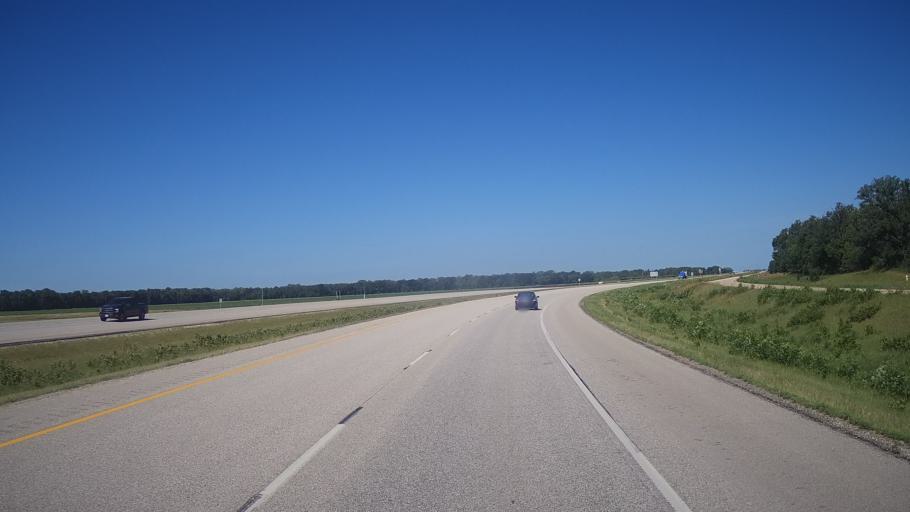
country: CA
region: Manitoba
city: Portage la Prairie
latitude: 49.9464
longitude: -98.2994
